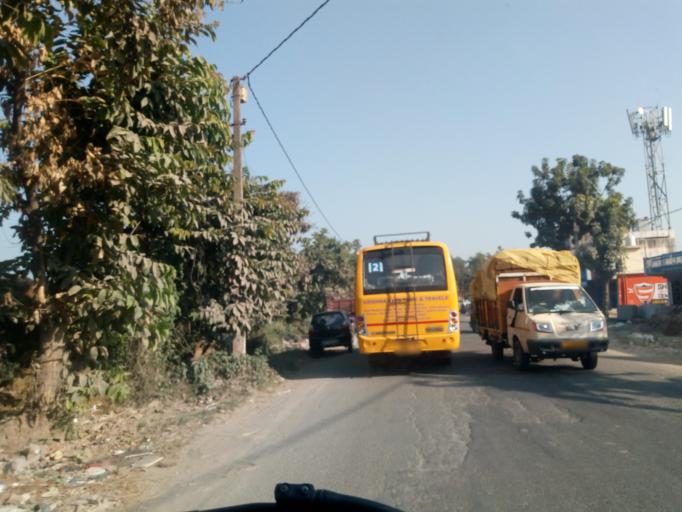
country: IN
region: Uttarakhand
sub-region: Dehradun
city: Vikasnagar
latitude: 30.3509
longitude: 77.8656
